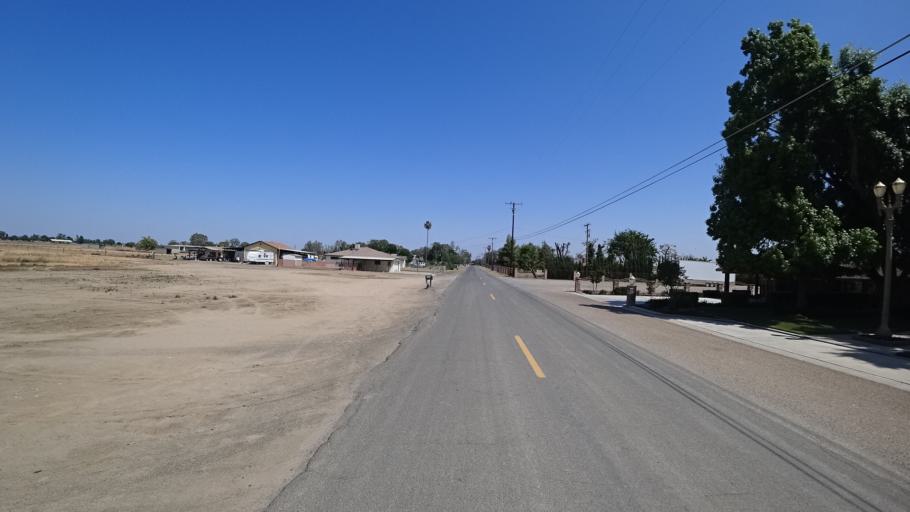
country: US
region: California
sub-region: Kings County
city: Home Garden
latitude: 36.3184
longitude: -119.6258
